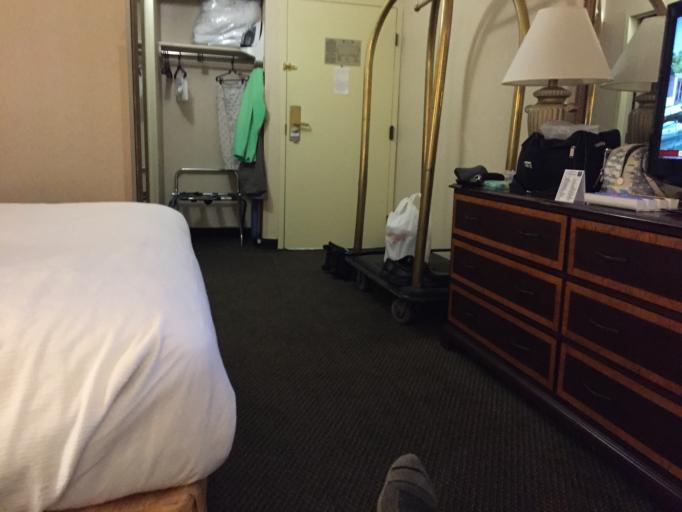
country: US
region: Ohio
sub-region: Hamilton County
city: Sharonville
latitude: 39.2898
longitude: -84.3986
